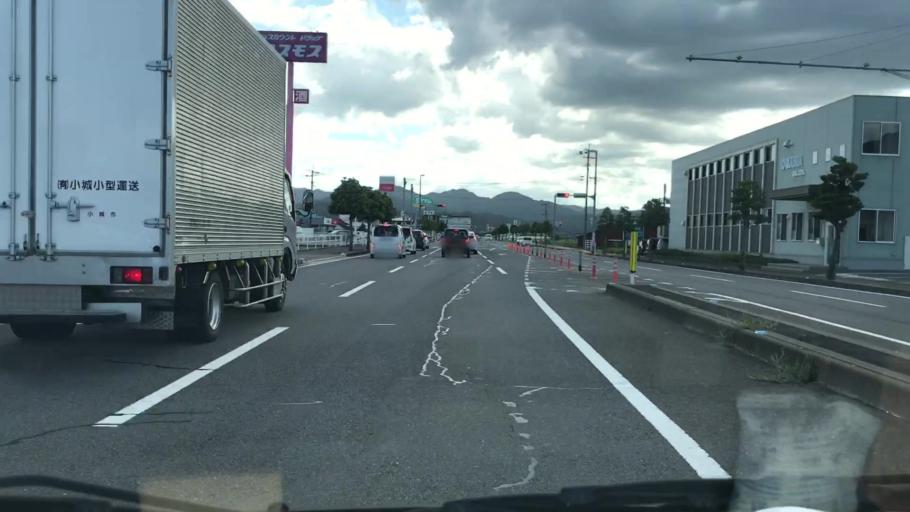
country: JP
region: Saga Prefecture
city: Kashima
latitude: 33.1263
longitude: 130.1019
